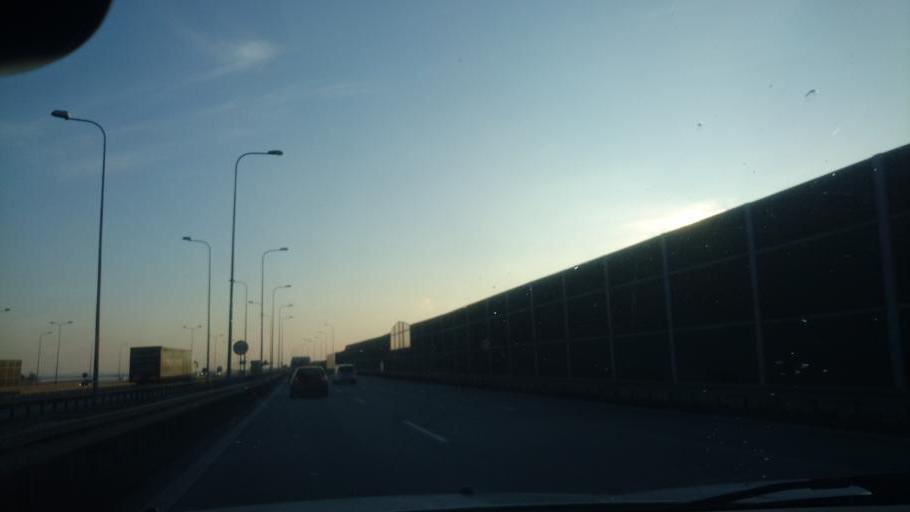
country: PL
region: Silesian Voivodeship
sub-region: Powiat gliwicki
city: Przyszowice
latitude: 50.2561
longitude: 18.7170
